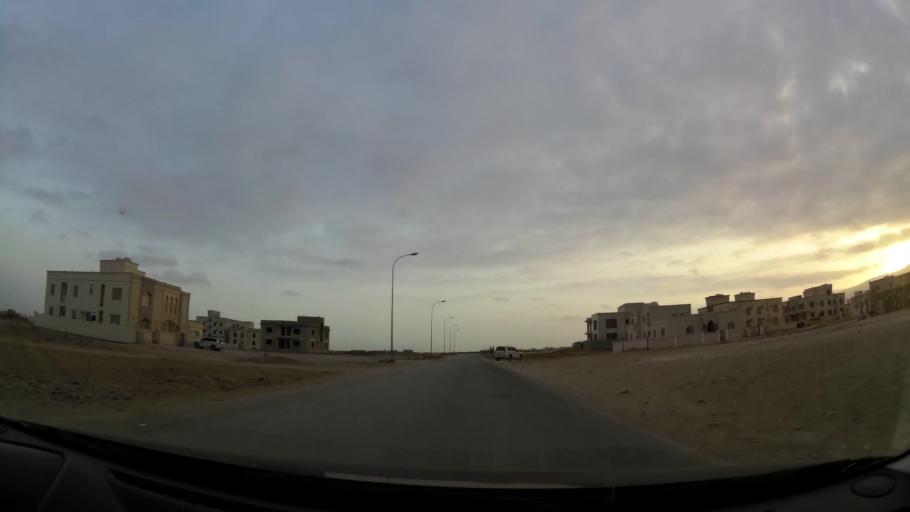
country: OM
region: Zufar
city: Salalah
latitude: 17.0265
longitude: 54.0112
